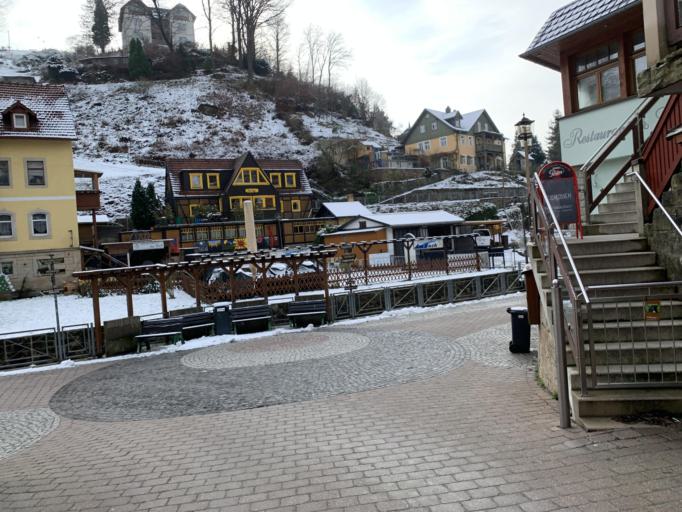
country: DE
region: Saxony
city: Hohnstein
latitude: 50.9589
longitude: 14.0827
